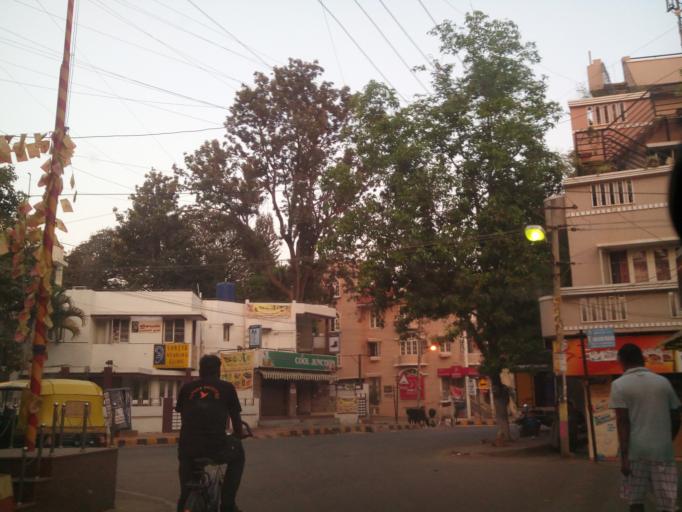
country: IN
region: Karnataka
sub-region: Bangalore Urban
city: Bangalore
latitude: 12.9272
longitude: 77.6380
